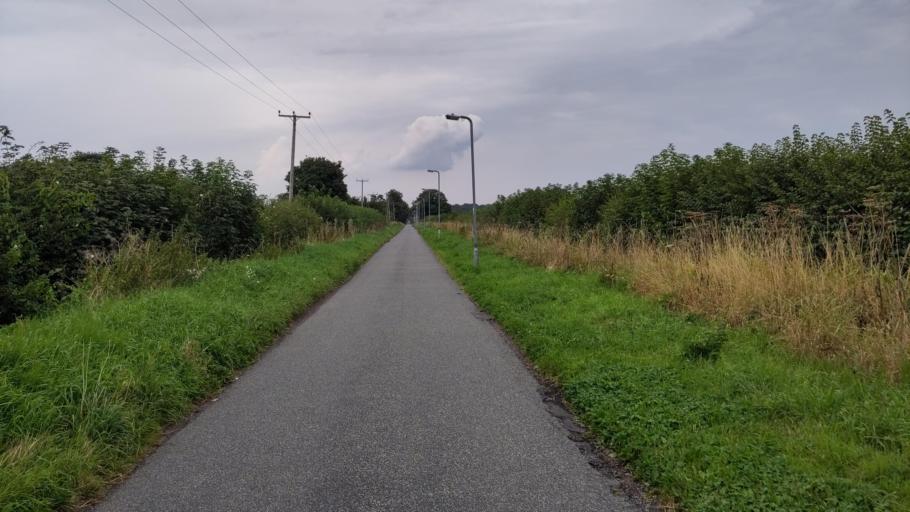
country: GB
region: England
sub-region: Cheshire West and Chester
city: Blacon
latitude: 53.1877
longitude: -2.9425
